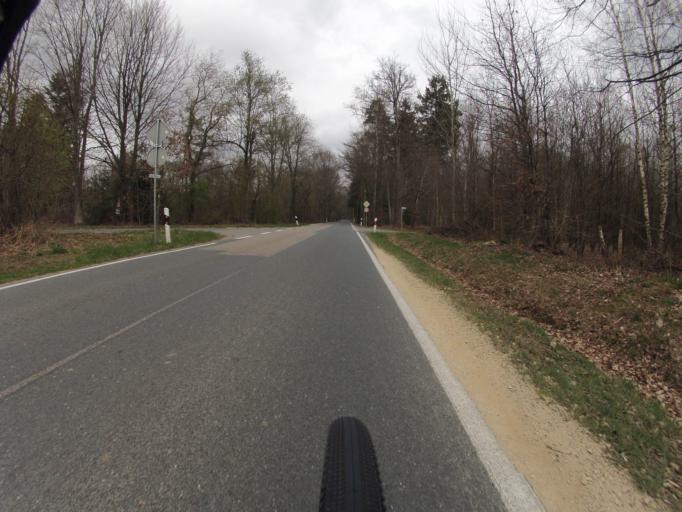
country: DE
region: North Rhine-Westphalia
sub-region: Regierungsbezirk Munster
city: Mettingen
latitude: 52.3056
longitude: 7.8190
